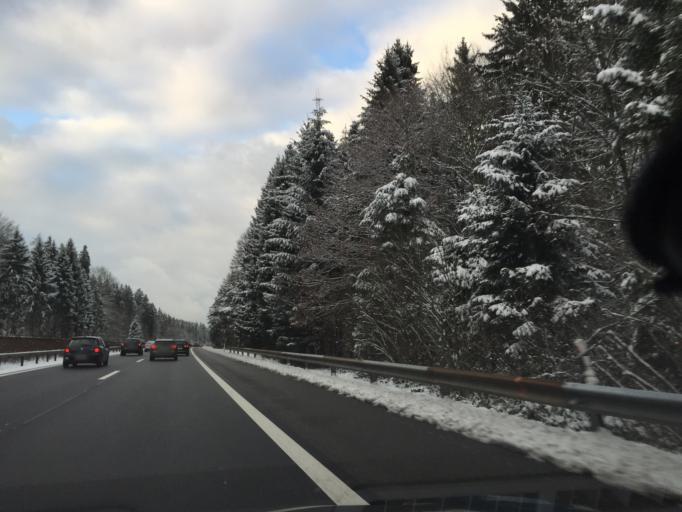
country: CH
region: Zurich
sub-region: Bezirk Horgen
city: Oberrieden / Mitte
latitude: 47.2624
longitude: 8.5777
